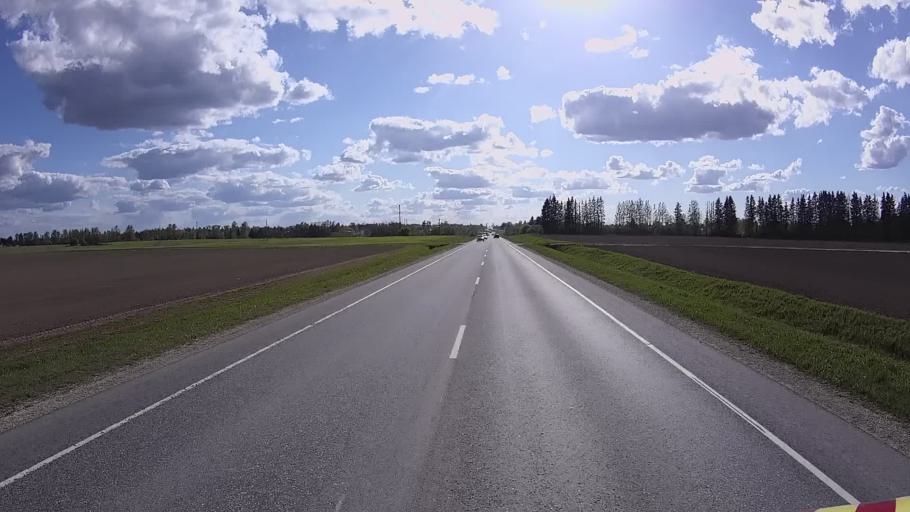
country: EE
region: Jogevamaa
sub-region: Jogeva linn
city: Jogeva
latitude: 58.7593
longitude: 26.4150
